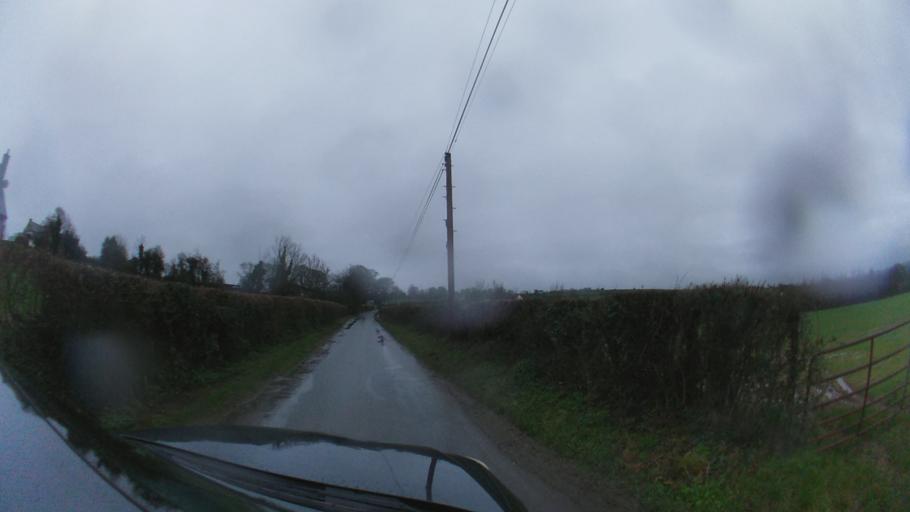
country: IE
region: Leinster
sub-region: Kilkenny
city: Graiguenamanagh
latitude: 52.5930
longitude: -6.9929
